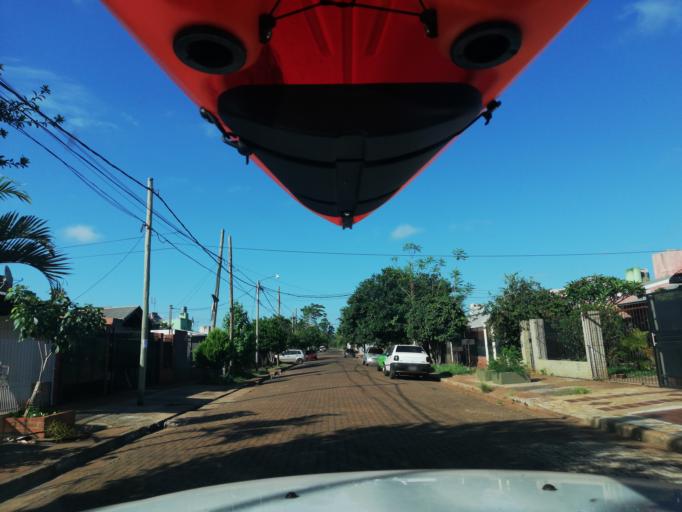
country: AR
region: Misiones
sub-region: Departamento de Capital
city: Posadas
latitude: -27.4242
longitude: -55.9385
